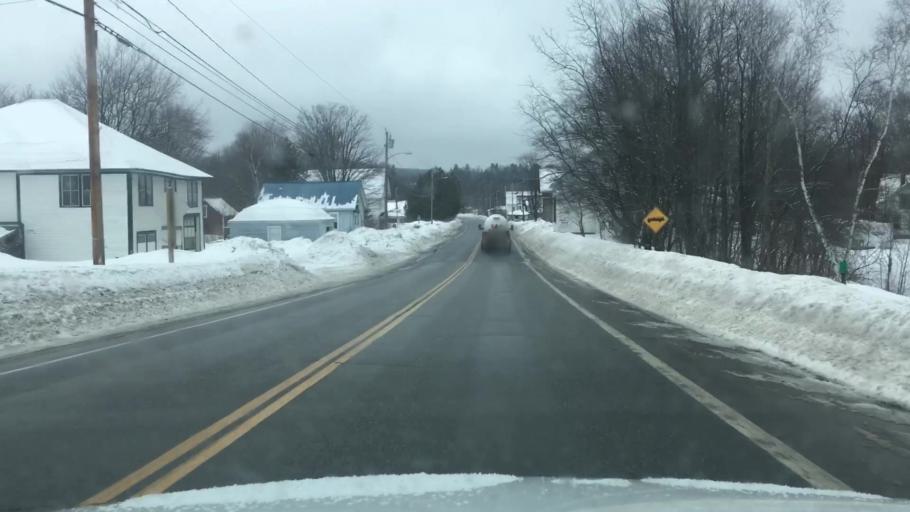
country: US
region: Maine
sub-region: Franklin County
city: Wilton
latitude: 44.5737
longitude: -70.3062
